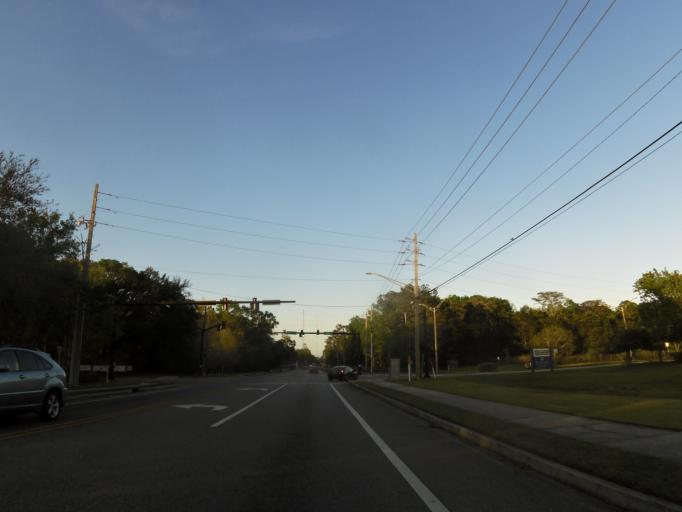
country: US
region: Florida
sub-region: Duval County
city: Jacksonville
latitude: 30.2563
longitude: -81.5822
